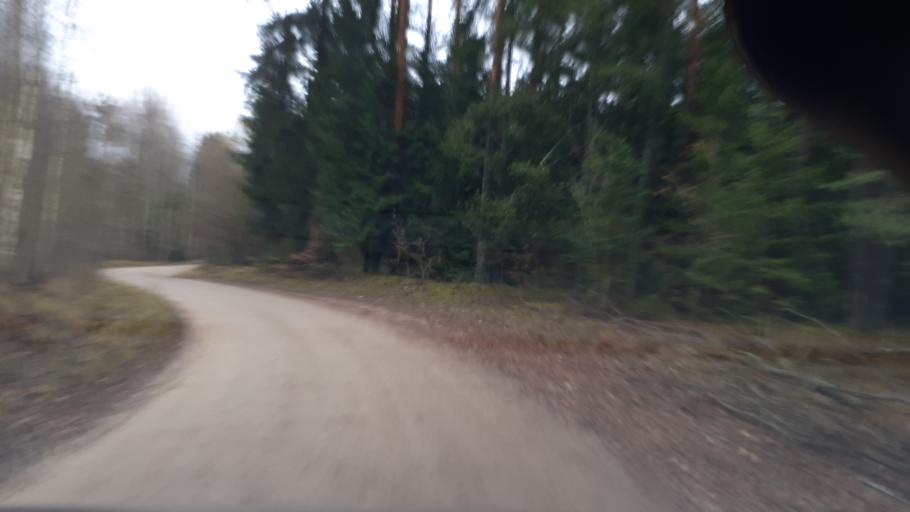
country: LV
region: Kuldigas Rajons
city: Kuldiga
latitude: 57.0251
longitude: 21.8681
